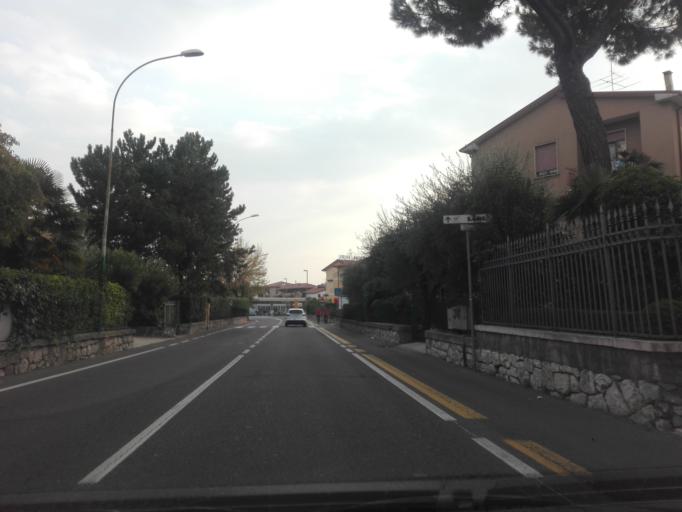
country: IT
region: Veneto
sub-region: Provincia di Verona
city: Bardolino
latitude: 45.5453
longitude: 10.7244
